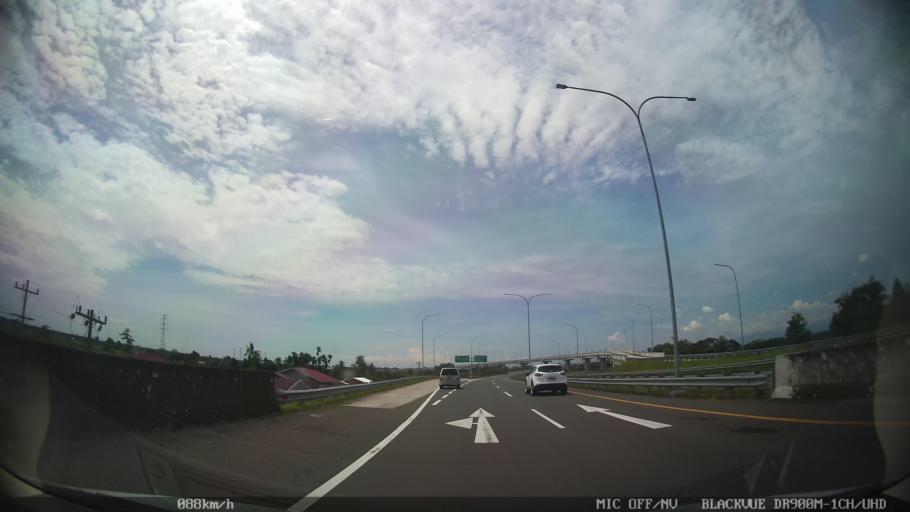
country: ID
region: North Sumatra
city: Percut
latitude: 3.5416
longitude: 98.8549
